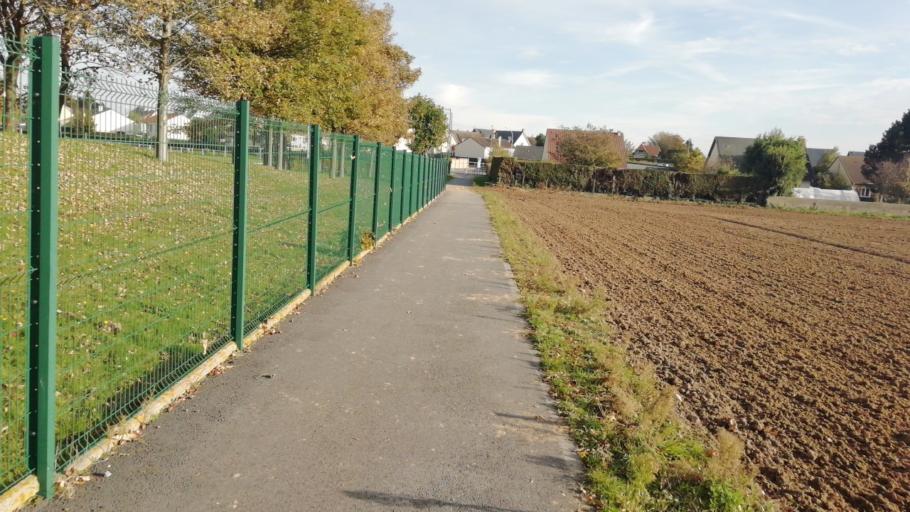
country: FR
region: Haute-Normandie
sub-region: Departement de la Seine-Maritime
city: Rogerville
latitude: 49.5069
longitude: 0.2629
